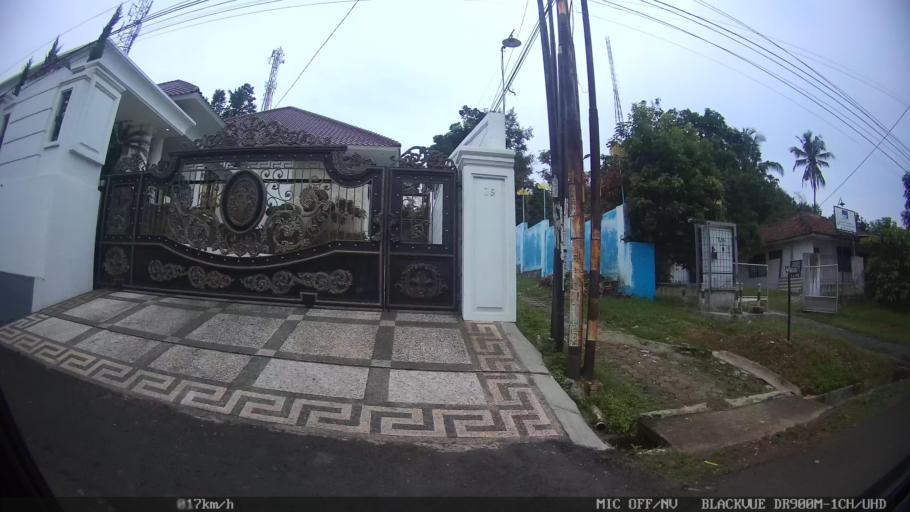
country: ID
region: Lampung
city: Kedaton
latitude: -5.4017
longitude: 105.2419
